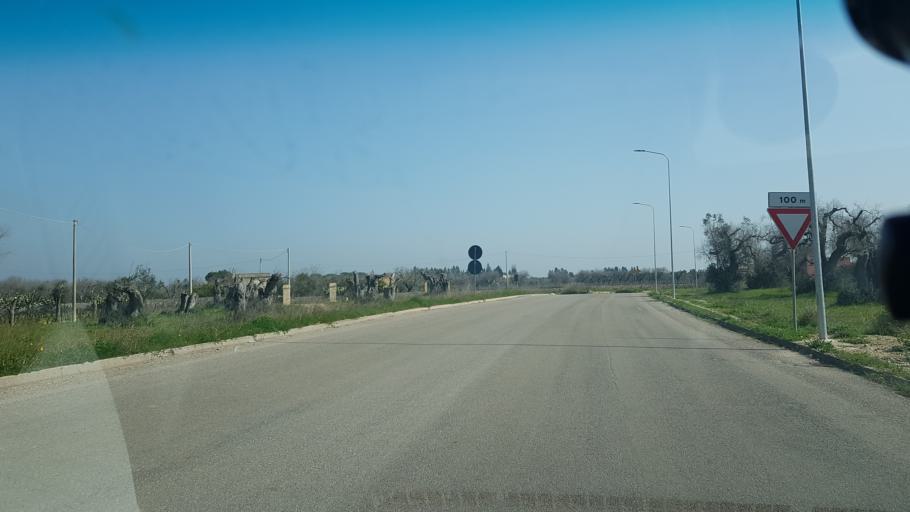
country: IT
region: Apulia
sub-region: Provincia di Lecce
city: Squinzano
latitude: 40.4487
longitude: 18.0397
